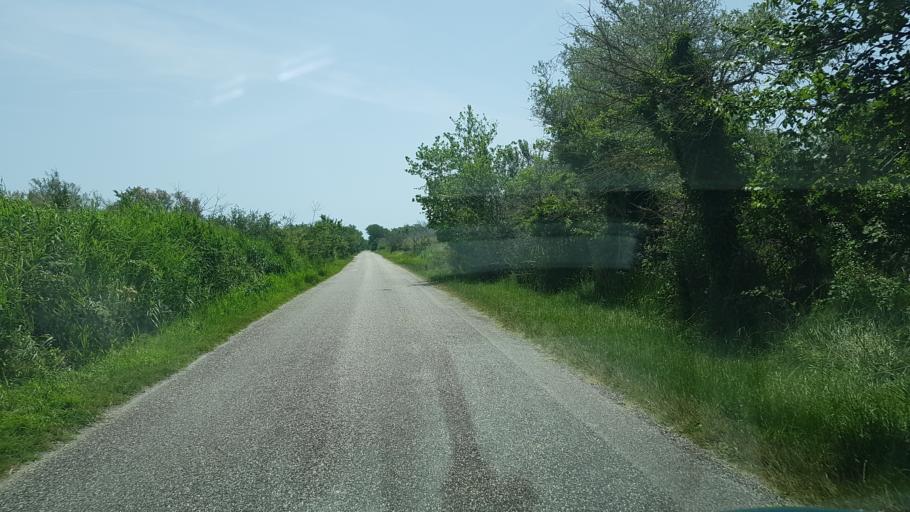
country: FR
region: Provence-Alpes-Cote d'Azur
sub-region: Departement des Bouches-du-Rhone
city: Port-Saint-Louis-du-Rhone
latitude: 43.4627
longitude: 4.6546
